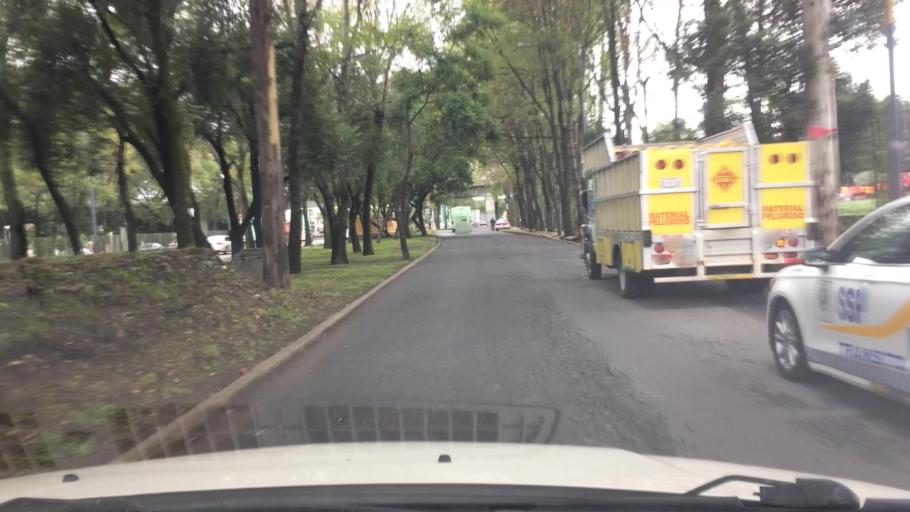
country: MX
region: Mexico City
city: Xochimilco
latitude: 19.2851
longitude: -99.1261
